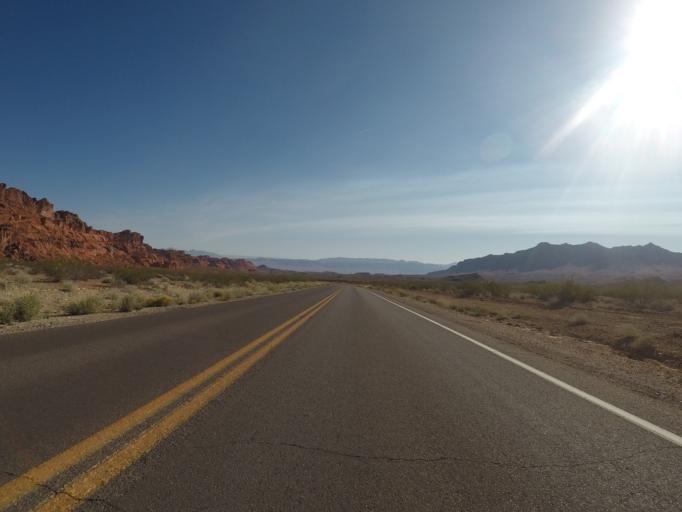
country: US
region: Nevada
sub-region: Clark County
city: Moapa Valley
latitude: 36.4257
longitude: -114.5380
